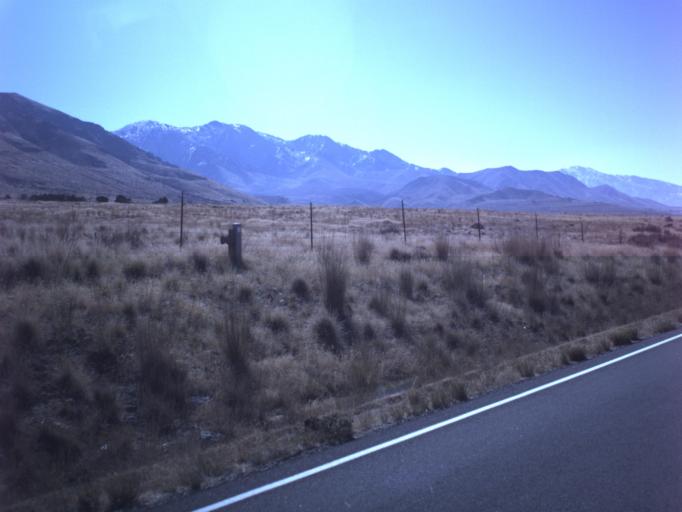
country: US
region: Utah
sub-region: Tooele County
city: Grantsville
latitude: 40.6716
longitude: -112.6737
